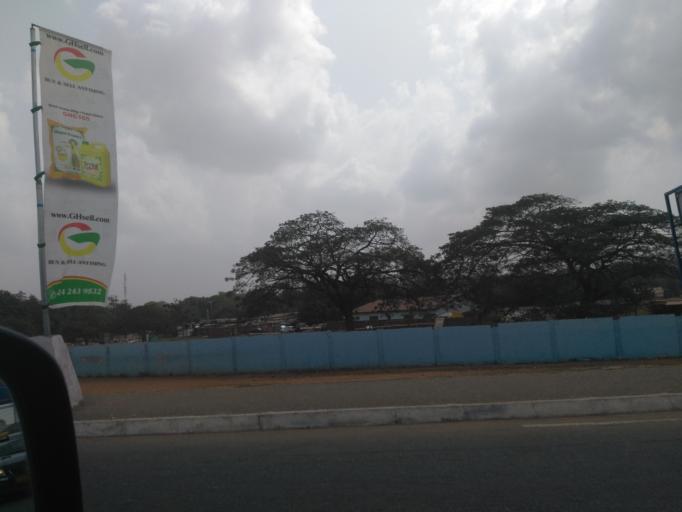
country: GH
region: Greater Accra
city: Accra
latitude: 5.5938
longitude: -0.1893
